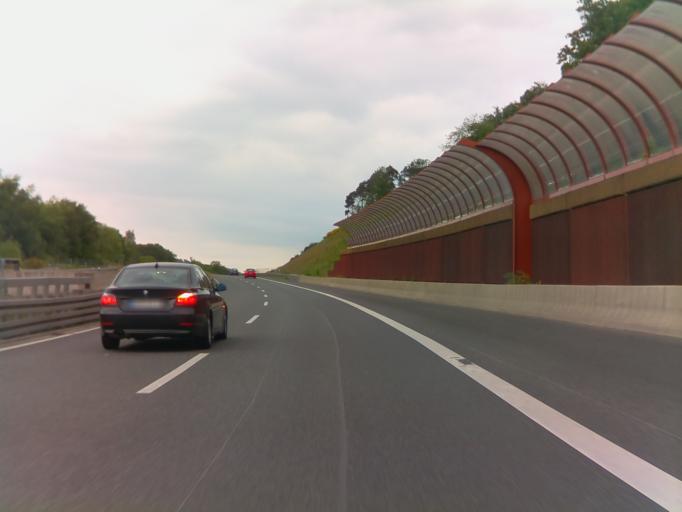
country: DE
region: Hesse
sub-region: Regierungsbezirk Giessen
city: Fronhausen
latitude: 50.7361
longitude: 8.7372
